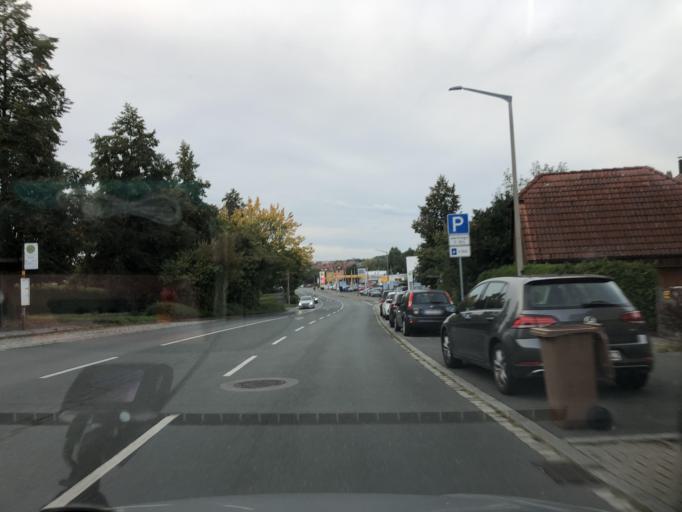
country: DE
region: Bavaria
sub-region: Regierungsbezirk Mittelfranken
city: Zirndorf
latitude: 49.4368
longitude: 10.9687
